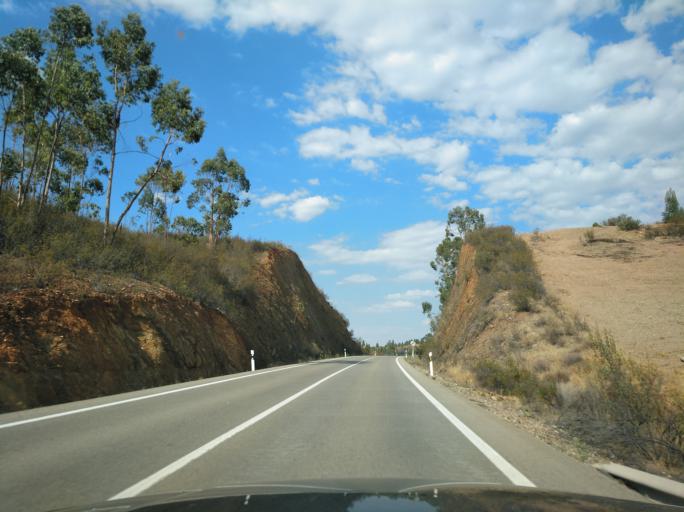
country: ES
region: Andalusia
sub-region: Provincia de Huelva
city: Santa Barbara de Casa
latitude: 37.8801
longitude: -7.2116
